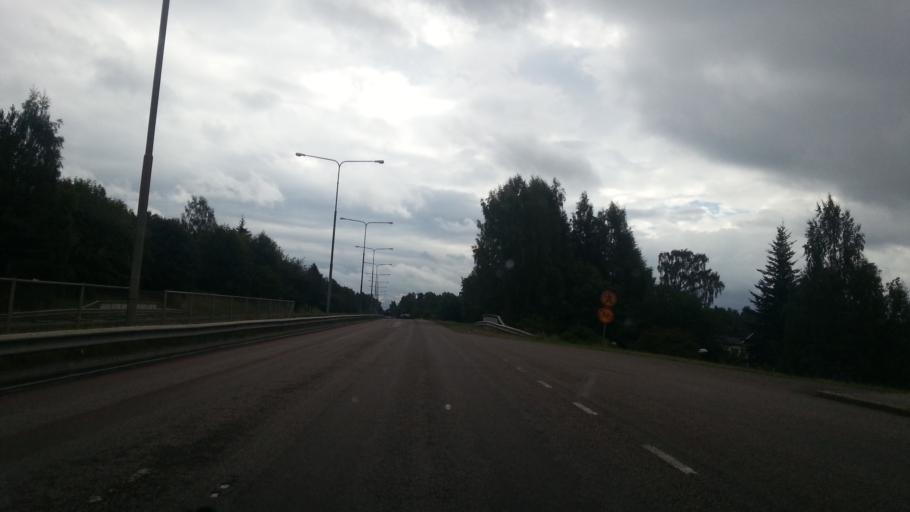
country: SE
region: Dalarna
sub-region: Faluns Kommun
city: Falun
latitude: 60.6014
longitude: 15.6581
